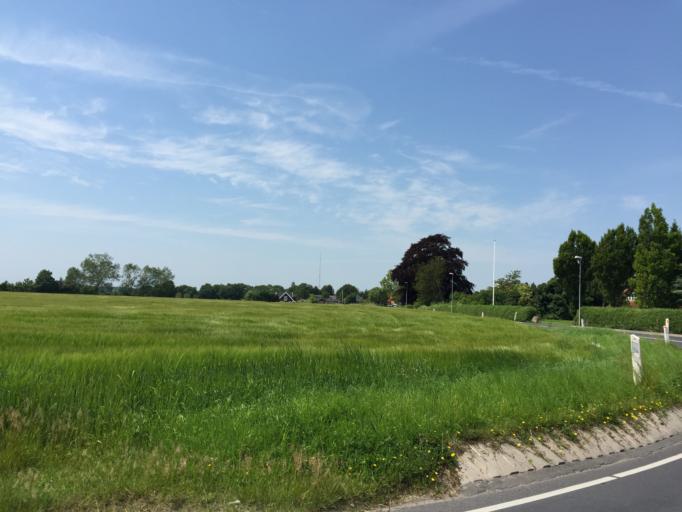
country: DK
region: South Denmark
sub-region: Kerteminde Kommune
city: Kerteminde
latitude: 55.4166
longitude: 10.6608
